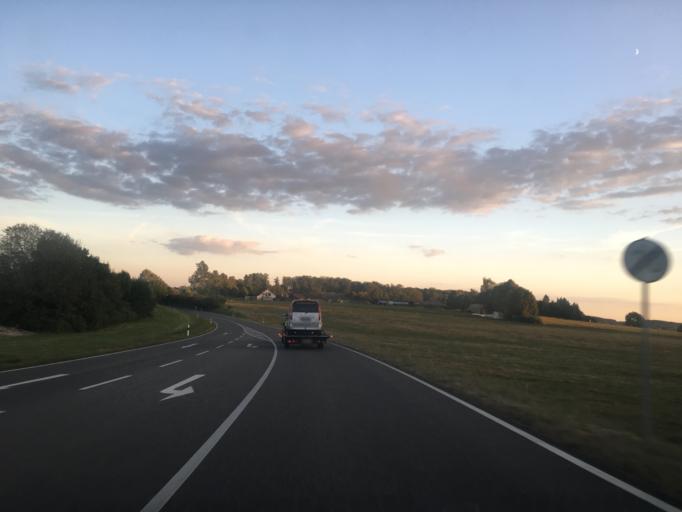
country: DE
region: Baden-Wuerttemberg
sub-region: Tuebingen Region
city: Gomadingen
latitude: 48.3571
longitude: 9.3276
